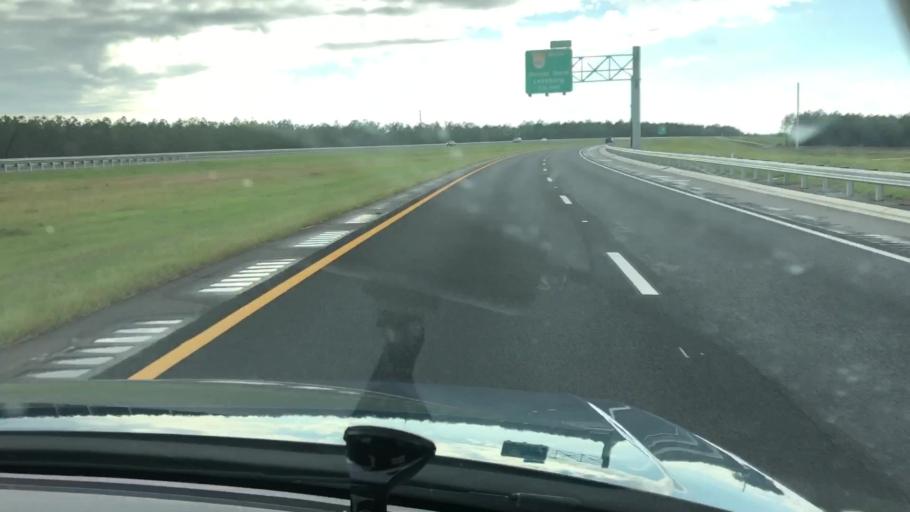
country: US
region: Florida
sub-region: Lake County
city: Mount Plymouth
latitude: 28.7777
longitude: -81.5270
